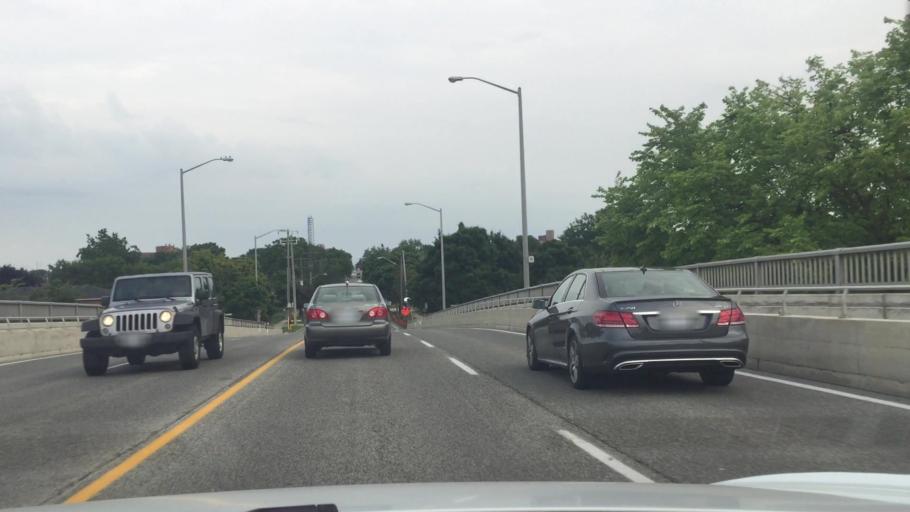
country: CA
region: Ontario
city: Scarborough
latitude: 43.7501
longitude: -79.3074
